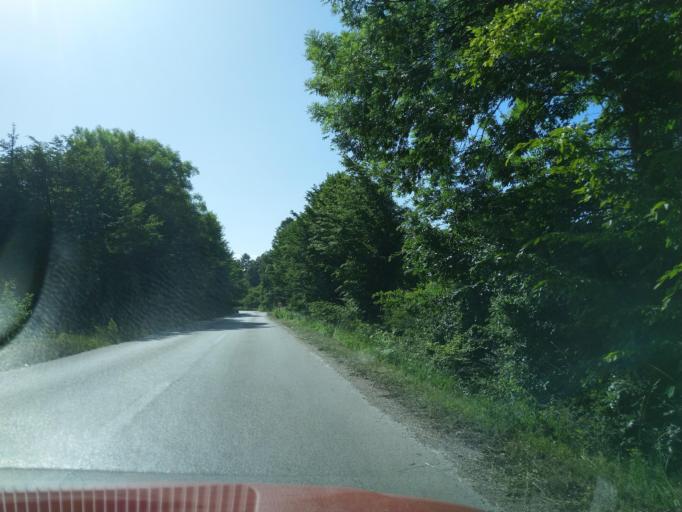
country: RS
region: Central Serbia
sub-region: Zlatiborski Okrug
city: Uzice
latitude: 43.8726
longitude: 19.7295
